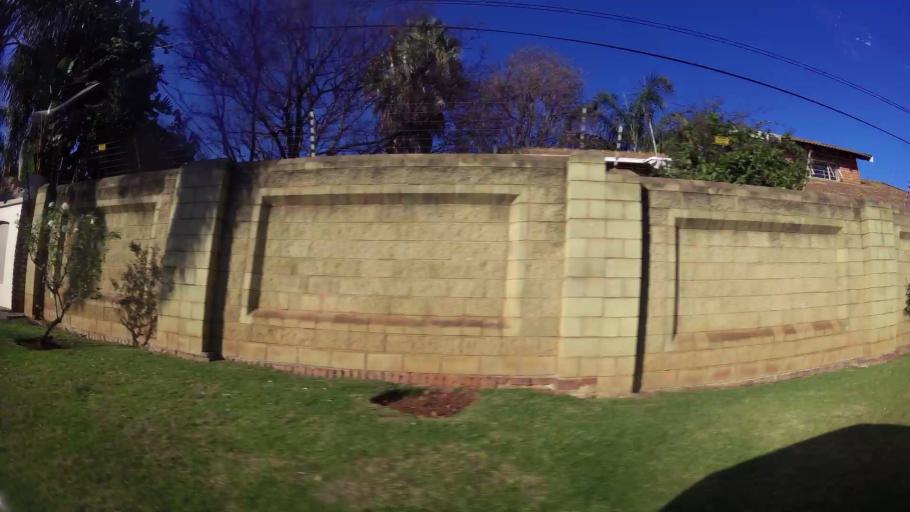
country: ZA
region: Gauteng
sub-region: City of Tshwane Metropolitan Municipality
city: Centurion
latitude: -25.8529
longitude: 28.1546
